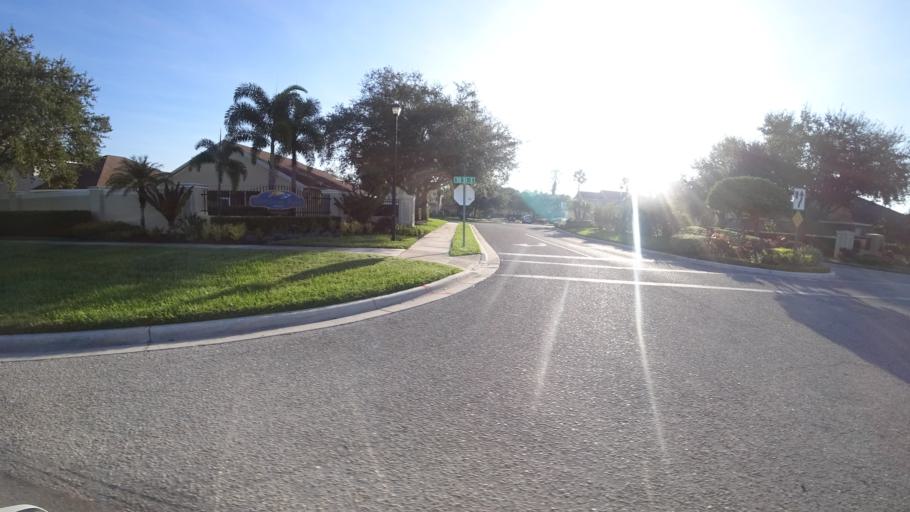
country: US
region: Florida
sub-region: Manatee County
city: Samoset
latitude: 27.4635
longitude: -82.5260
